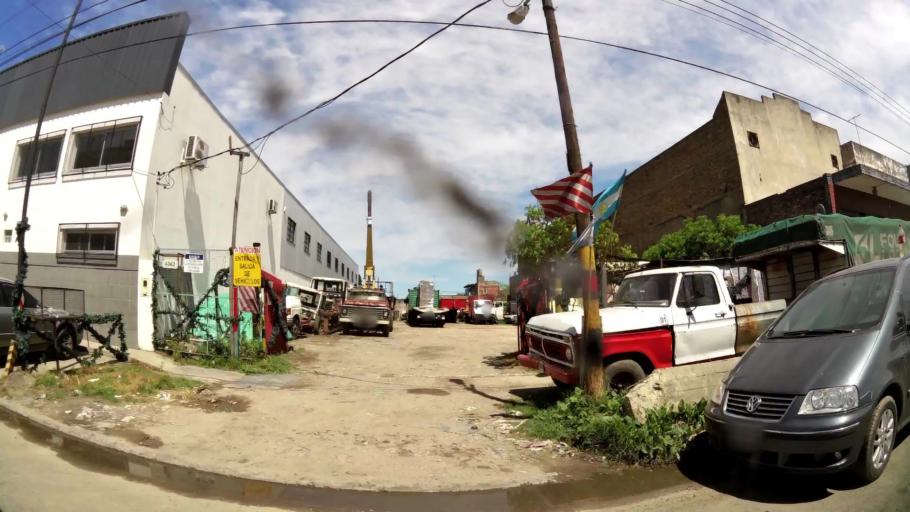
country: AR
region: Buenos Aires
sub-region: Partido de Quilmes
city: Quilmes
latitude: -34.7473
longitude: -58.3009
